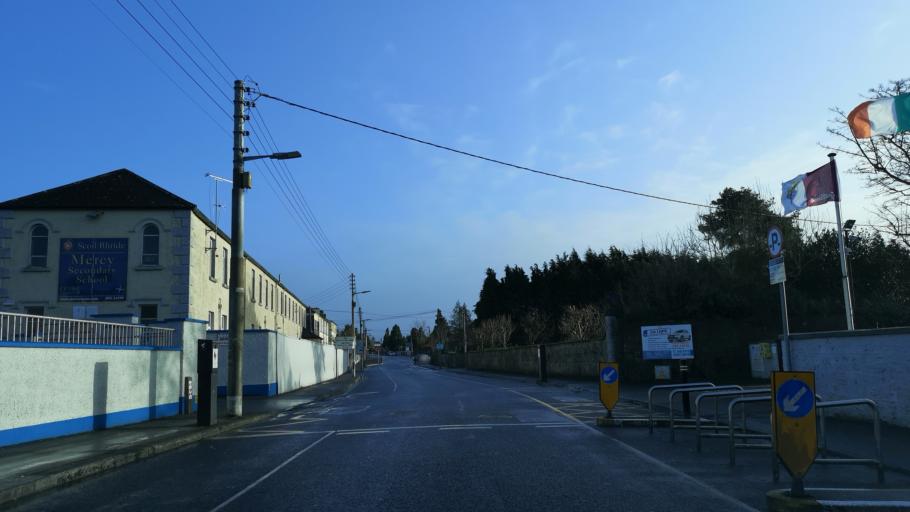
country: IE
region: Connaught
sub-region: County Galway
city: Tuam
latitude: 53.5131
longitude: -8.8487
